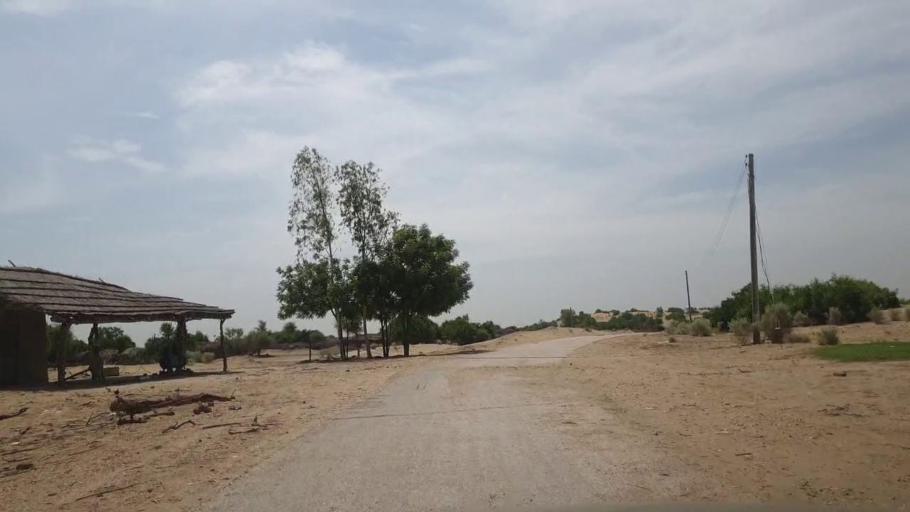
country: PK
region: Sindh
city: Kot Diji
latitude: 27.1089
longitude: 69.0767
